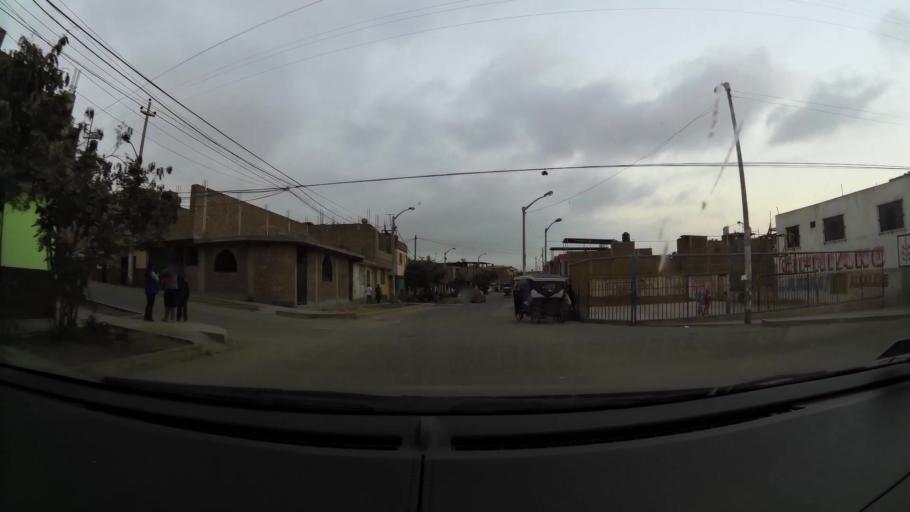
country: PE
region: La Libertad
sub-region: Provincia de Trujillo
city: El Porvenir
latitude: -8.0810
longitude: -79.0179
